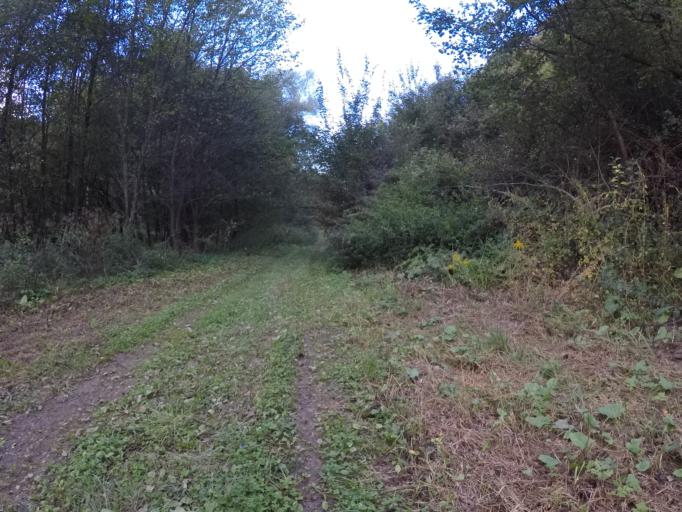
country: SK
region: Presovsky
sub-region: Okres Presov
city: Presov
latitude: 48.9312
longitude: 21.1672
